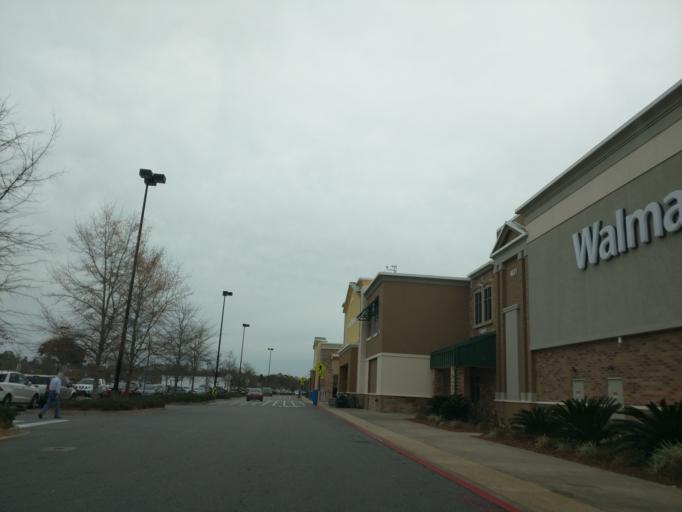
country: US
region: Florida
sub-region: Leon County
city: Tallahassee
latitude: 30.4613
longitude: -84.2175
